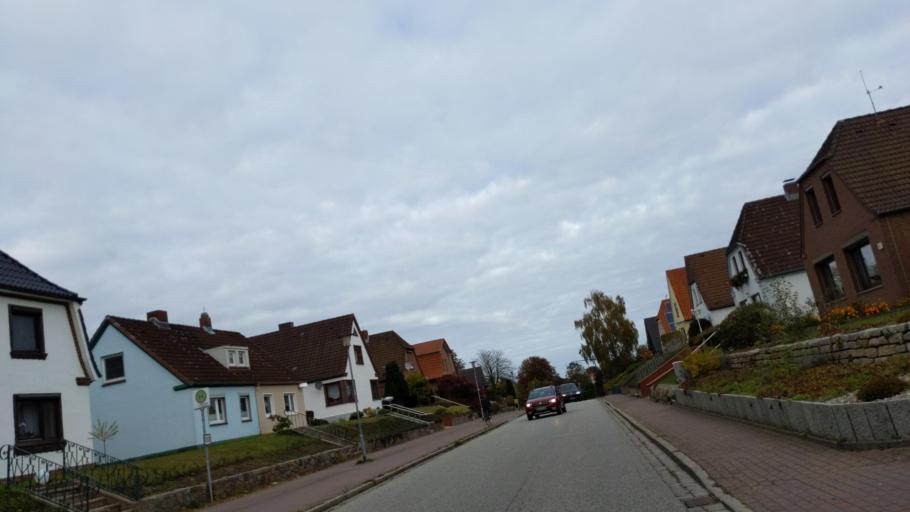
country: DE
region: Schleswig-Holstein
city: Neustadt in Holstein
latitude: 54.1140
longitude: 10.8222
